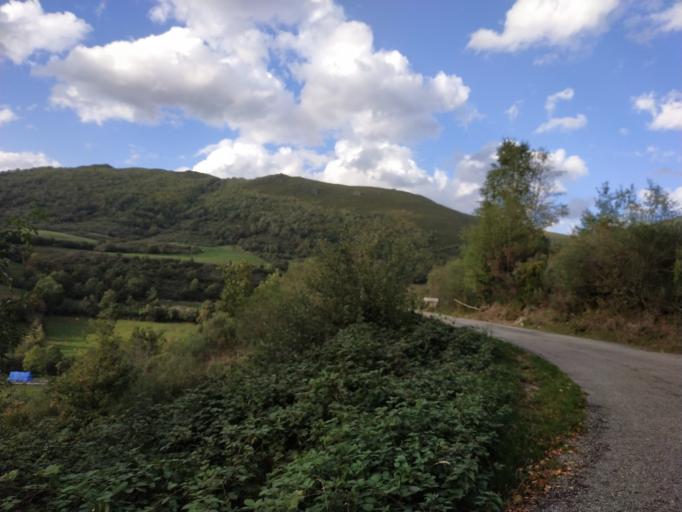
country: ES
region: Castille and Leon
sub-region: Provincia de Leon
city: Candin
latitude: 42.8643
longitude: -6.8522
